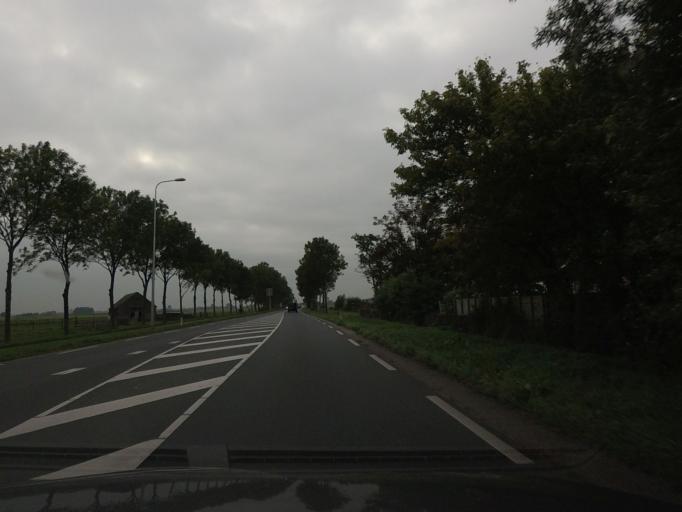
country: NL
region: North Holland
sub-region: Gemeente Opmeer
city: Opmeer
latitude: 52.7078
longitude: 4.9330
